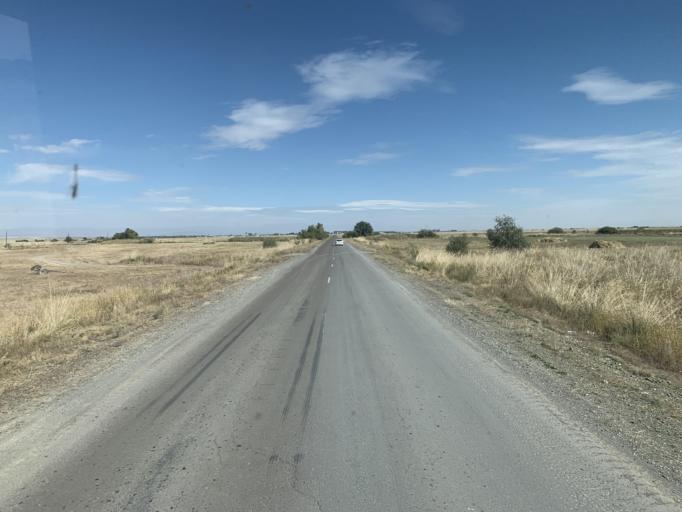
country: CN
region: Xinjiang Uygur Zizhiqu
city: Tacheng
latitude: 46.6631
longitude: 82.7497
